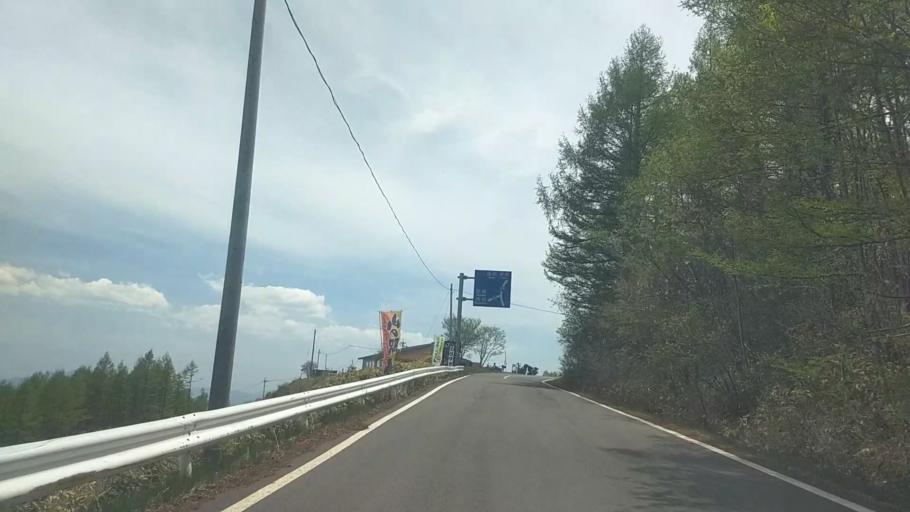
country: JP
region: Nagano
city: Saku
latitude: 36.0649
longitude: 138.3915
